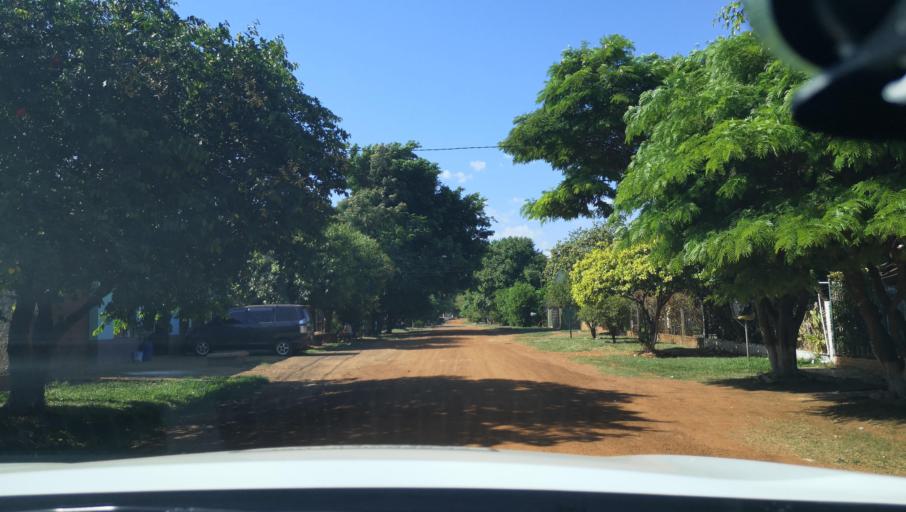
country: PY
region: Itapua
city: Carmen del Parana
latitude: -27.1674
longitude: -56.2348
